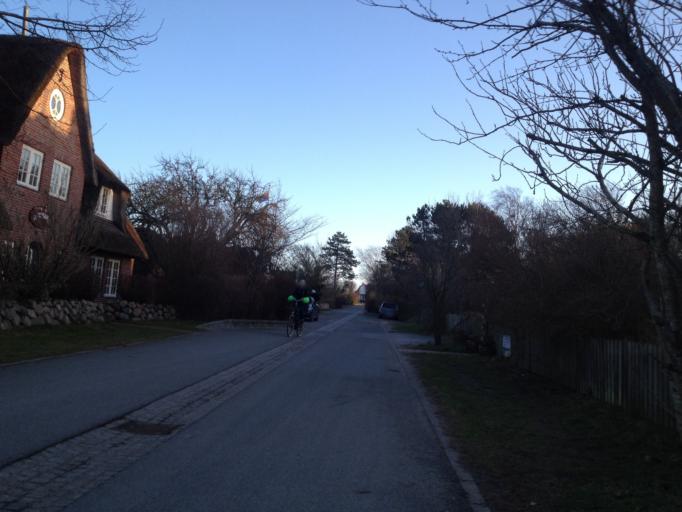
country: DE
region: Schleswig-Holstein
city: Nebel
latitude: 54.6502
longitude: 8.3569
